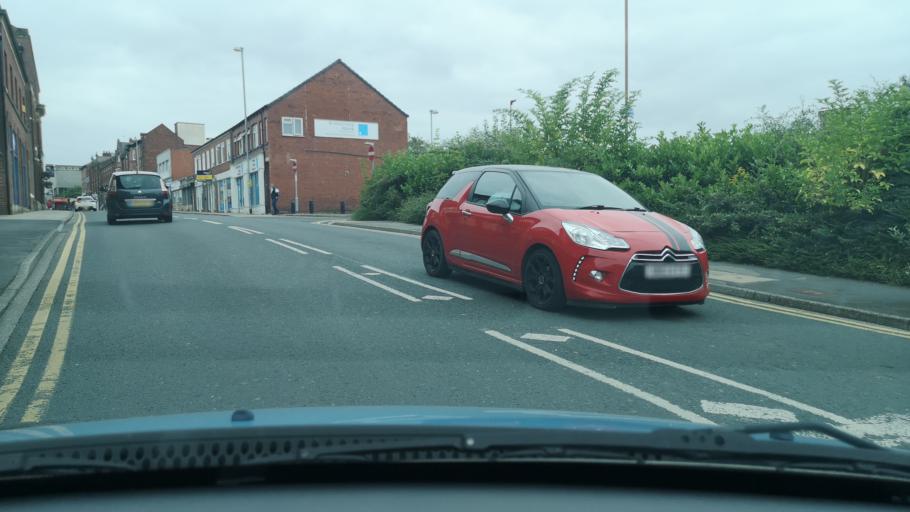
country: GB
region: England
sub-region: City and Borough of Wakefield
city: Castleford
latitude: 53.7277
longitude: -1.3540
